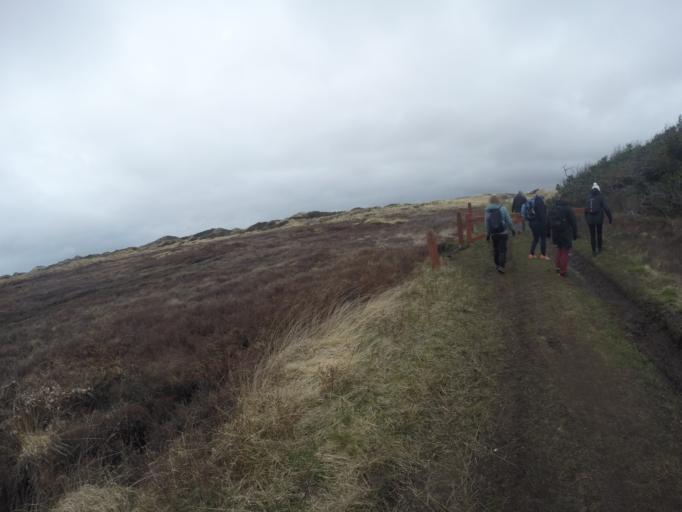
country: DK
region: North Denmark
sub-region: Thisted Kommune
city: Hurup
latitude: 56.8625
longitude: 8.2918
